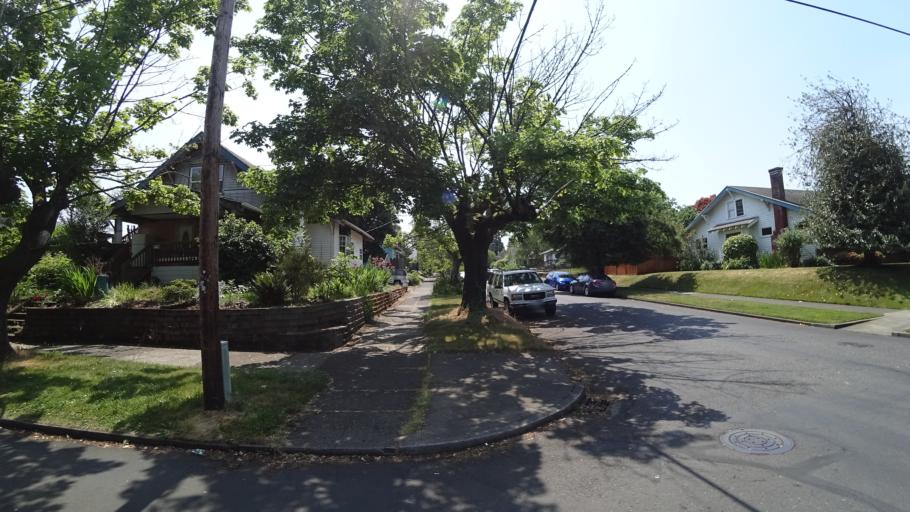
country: US
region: Oregon
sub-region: Multnomah County
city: Portland
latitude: 45.5803
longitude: -122.6847
